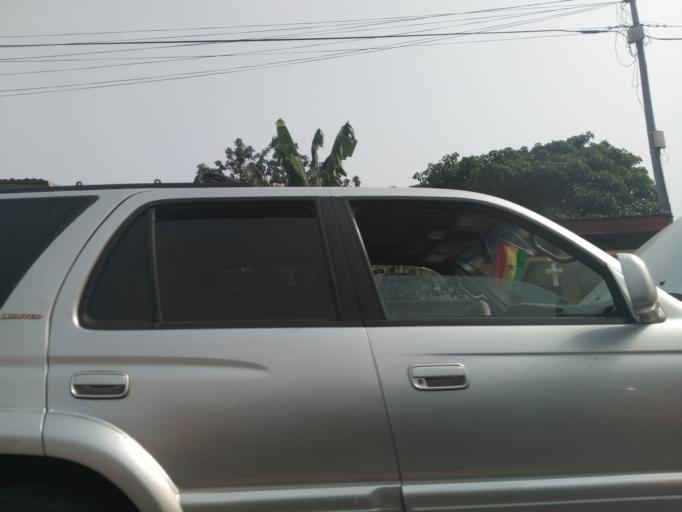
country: GH
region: Ashanti
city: Kumasi
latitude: 6.6834
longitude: -1.6092
